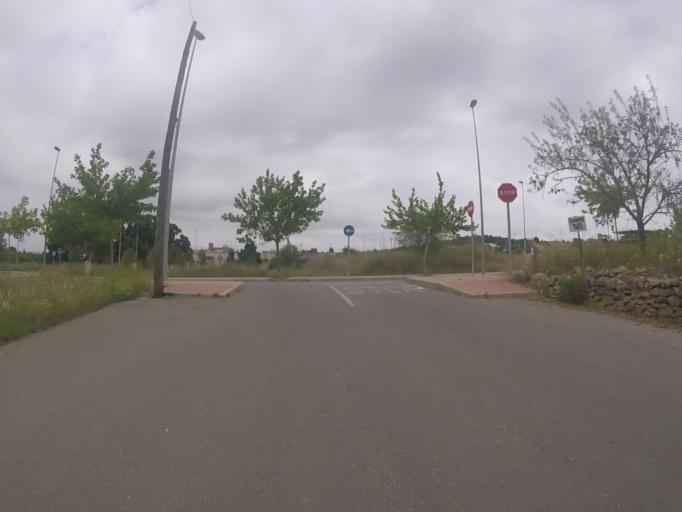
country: ES
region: Valencia
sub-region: Provincia de Castello
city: Cabanes
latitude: 40.1509
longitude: 0.0474
